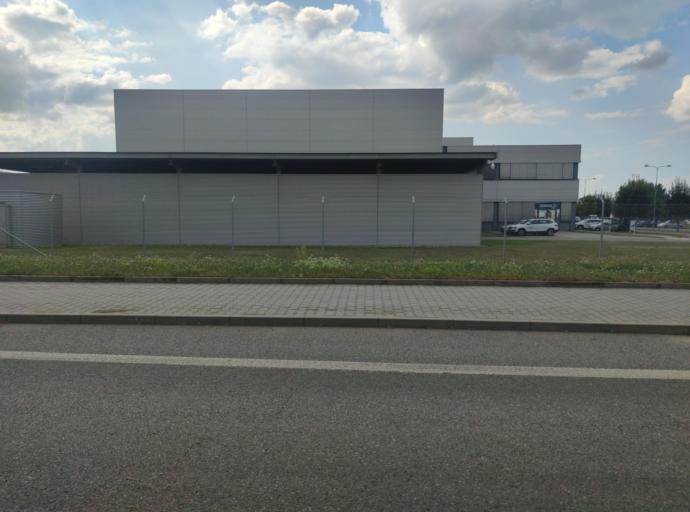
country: CZ
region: South Moravian
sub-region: Mesto Brno
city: Brno
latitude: 49.1831
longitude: 16.6566
